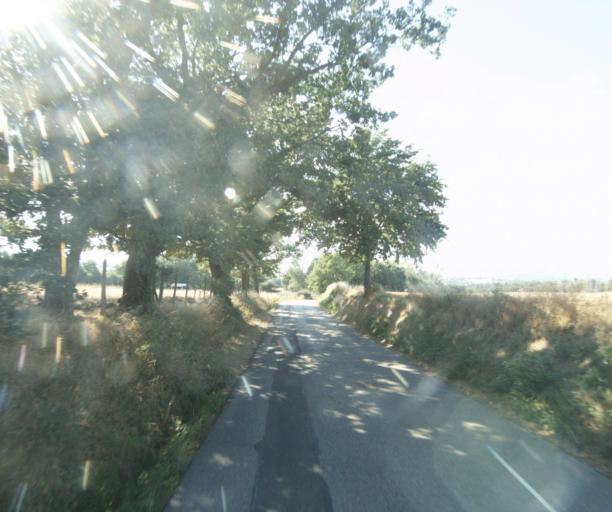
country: FR
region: Rhone-Alpes
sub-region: Departement du Rhone
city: Lentilly
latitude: 45.8139
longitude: 4.6750
